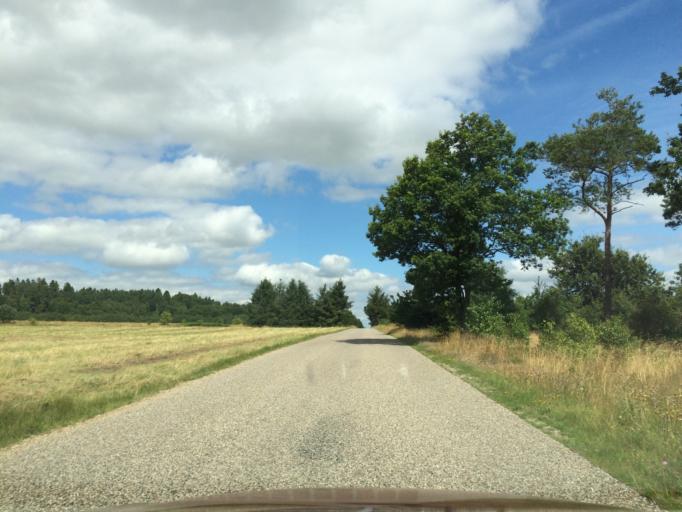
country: DK
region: Central Jutland
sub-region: Silkeborg Kommune
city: Svejbaek
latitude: 56.1878
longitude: 9.6426
